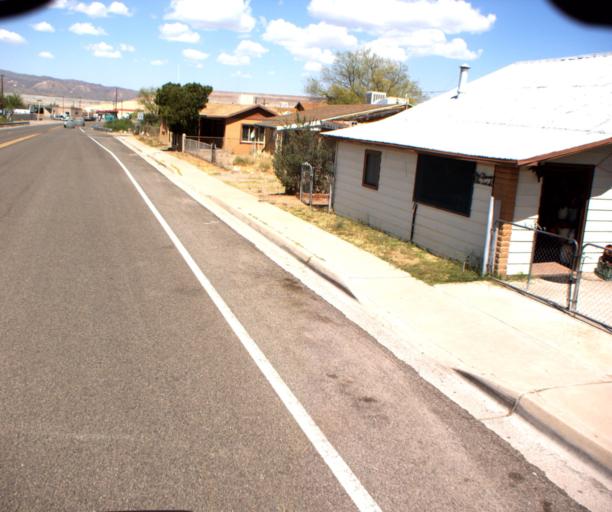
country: US
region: Arizona
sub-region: Pinal County
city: Kearny
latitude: 32.9878
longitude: -110.7736
